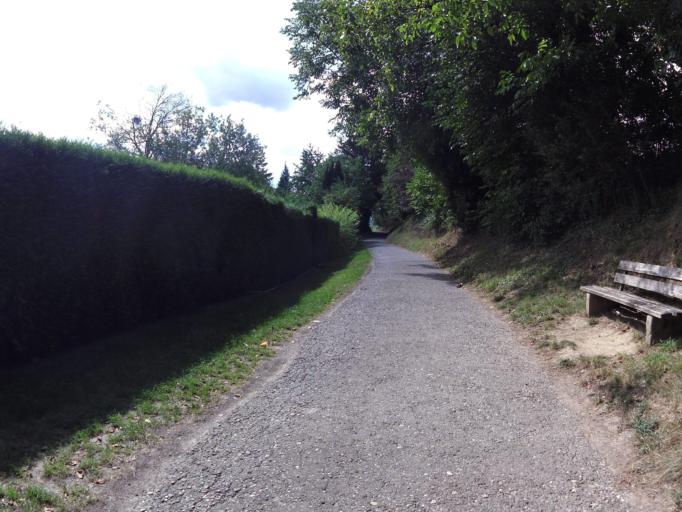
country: DE
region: Baden-Wuerttemberg
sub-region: Freiburg Region
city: Lahr
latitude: 48.3275
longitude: 7.8672
